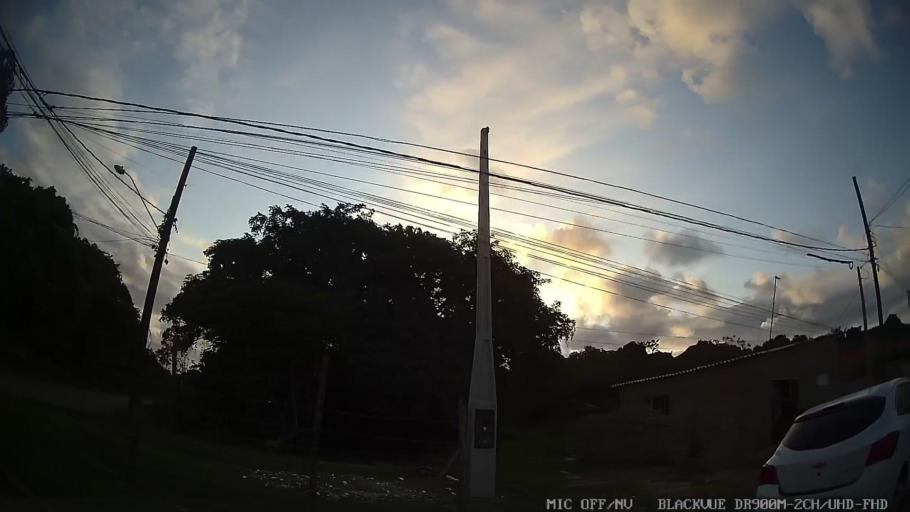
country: BR
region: Sao Paulo
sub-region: Itanhaem
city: Itanhaem
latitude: -24.1862
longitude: -46.8256
